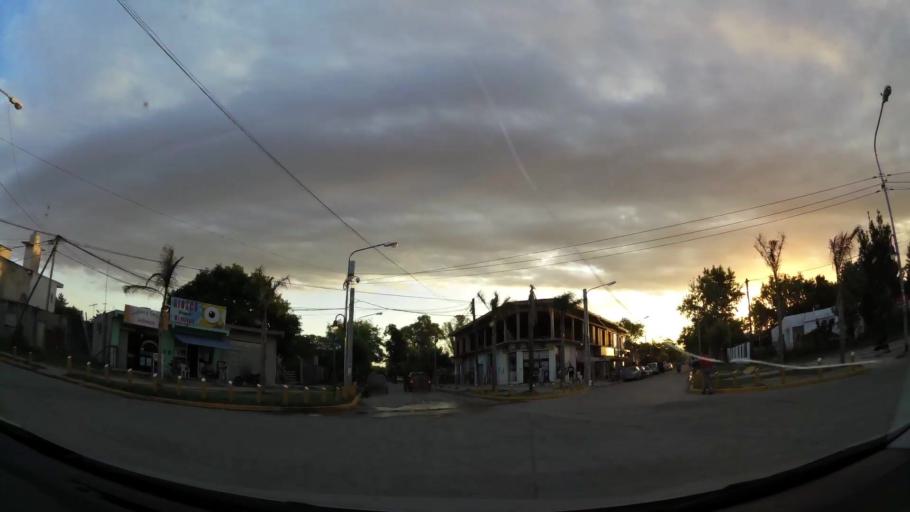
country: AR
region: Buenos Aires
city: Santa Catalina - Dique Lujan
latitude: -34.4378
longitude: -58.6667
